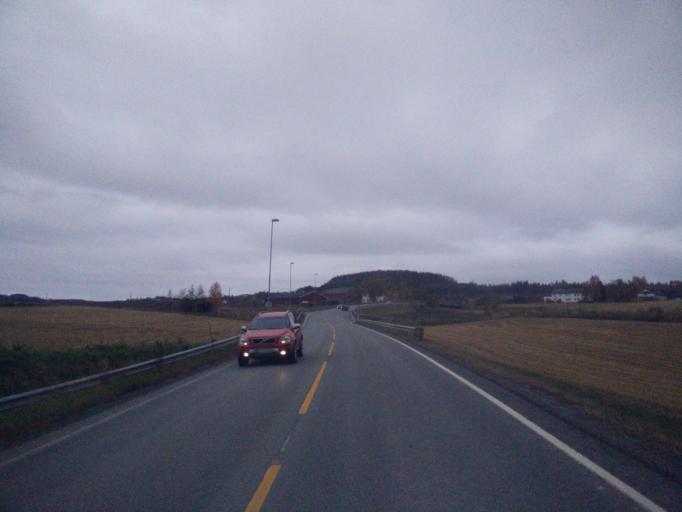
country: NO
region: Nord-Trondelag
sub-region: Stjordal
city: Stjordal
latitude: 63.5020
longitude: 10.8619
